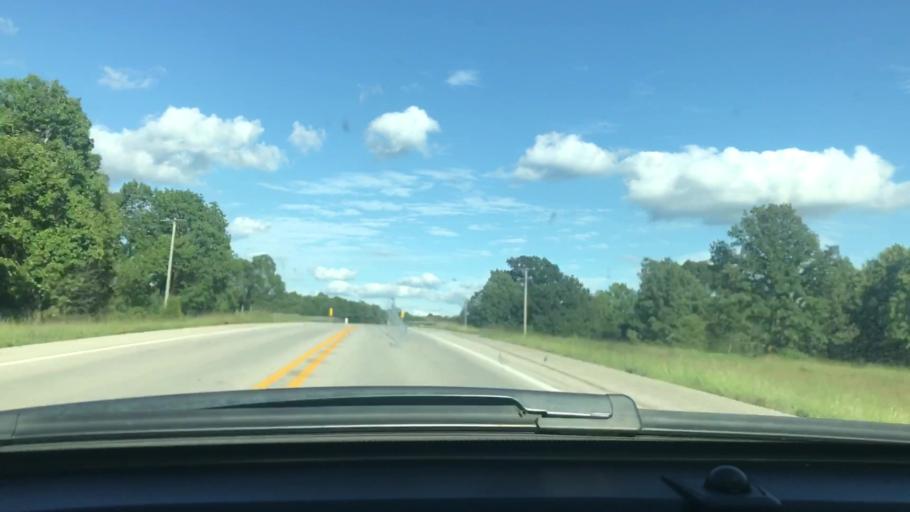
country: US
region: Missouri
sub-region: Howell County
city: West Plains
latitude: 36.6606
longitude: -91.7159
